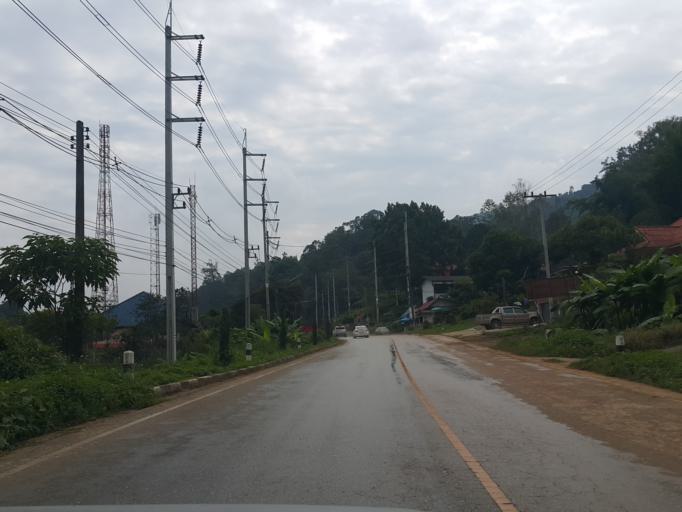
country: TH
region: Chiang Mai
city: Mae Taeng
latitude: 19.1641
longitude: 98.6905
